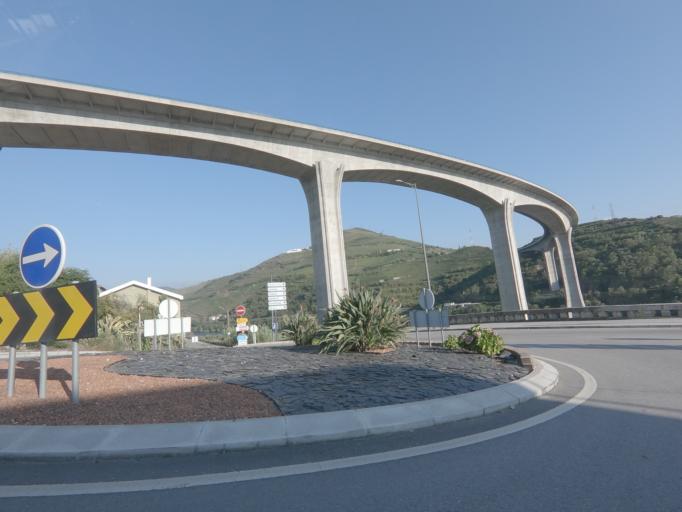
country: PT
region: Vila Real
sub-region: Peso da Regua
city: Peso da Regua
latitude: 41.1560
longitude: -7.7774
